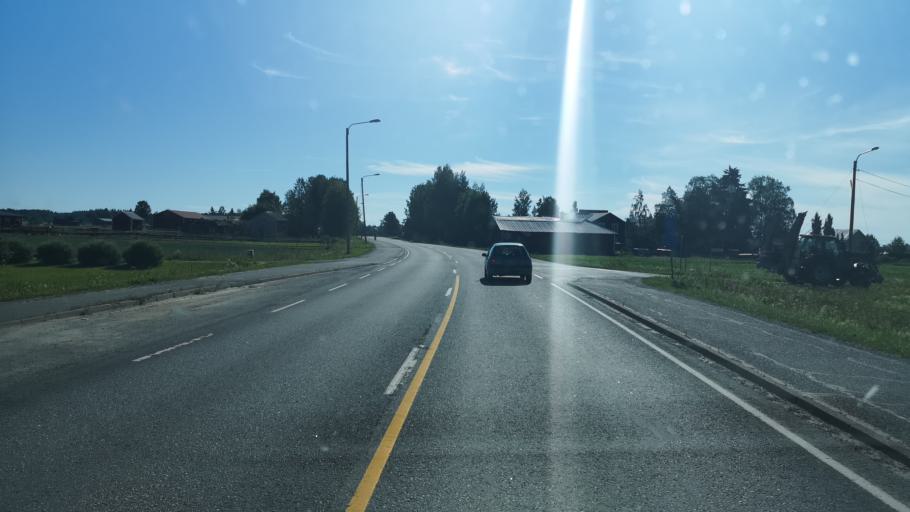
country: FI
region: Southern Ostrobothnia
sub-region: Seinaejoki
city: Lapua
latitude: 62.9697
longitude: 23.0748
